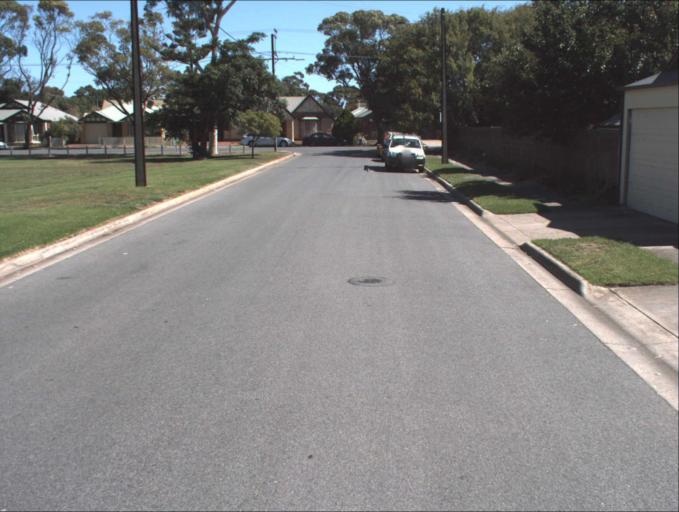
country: AU
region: South Australia
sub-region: Port Adelaide Enfield
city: Alberton
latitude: -34.8633
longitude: 138.5206
